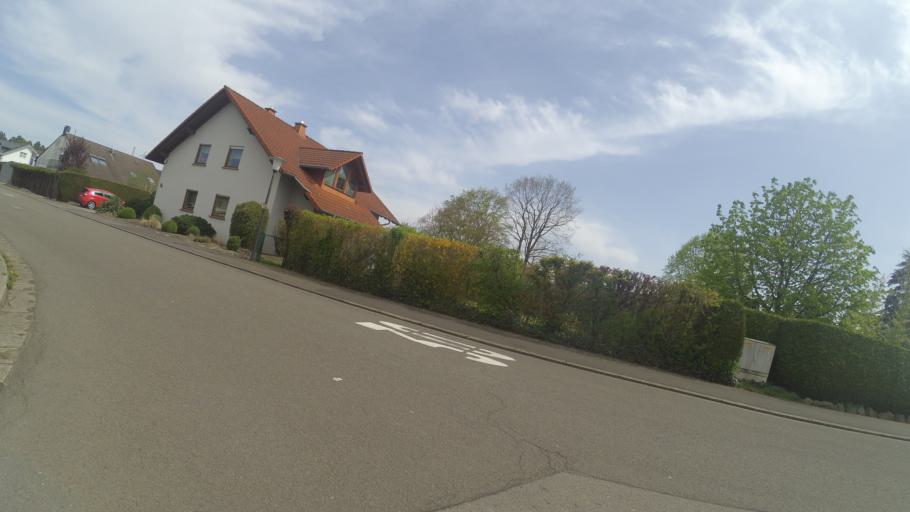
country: DE
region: Saarland
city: Homburg
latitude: 49.3506
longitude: 7.3256
